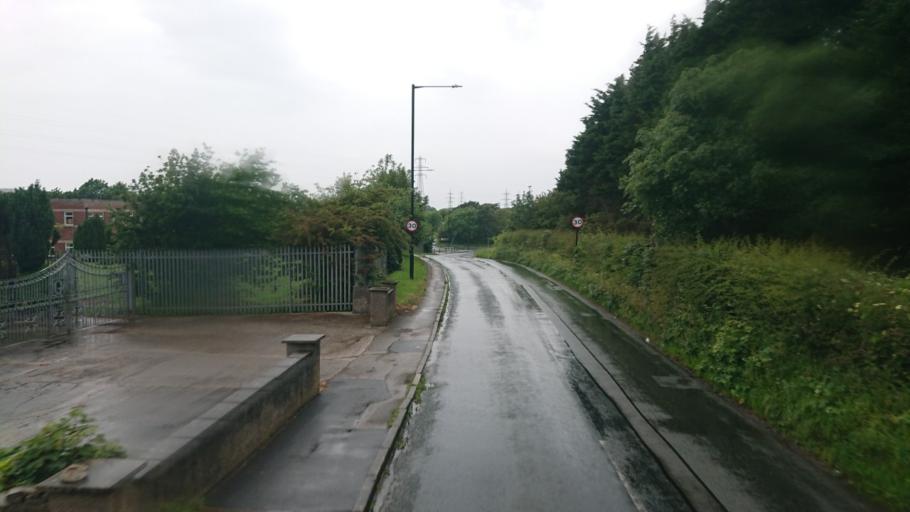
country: GB
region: England
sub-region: Lancashire
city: Morecambe
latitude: 54.0239
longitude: -2.8845
